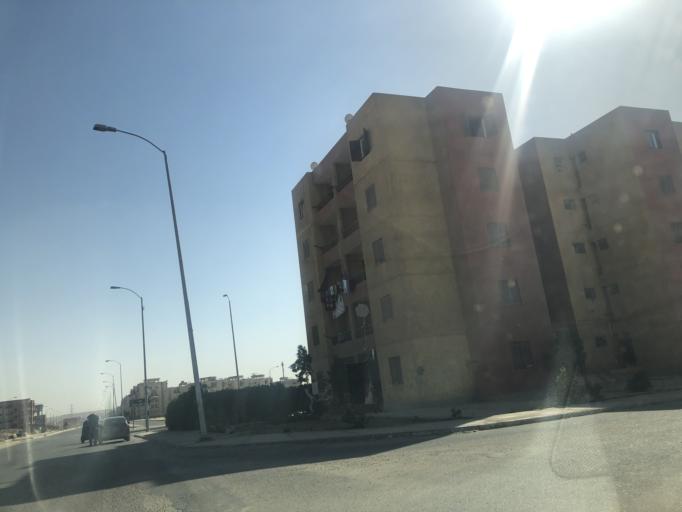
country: EG
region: Al Jizah
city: Madinat Sittah Uktubar
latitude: 29.9232
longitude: 30.9379
